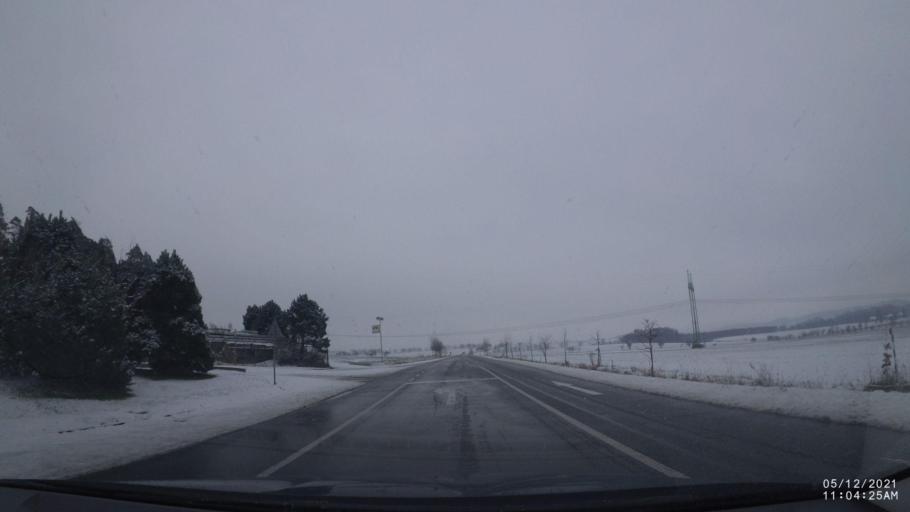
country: CZ
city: Solnice
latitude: 50.1708
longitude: 16.2211
